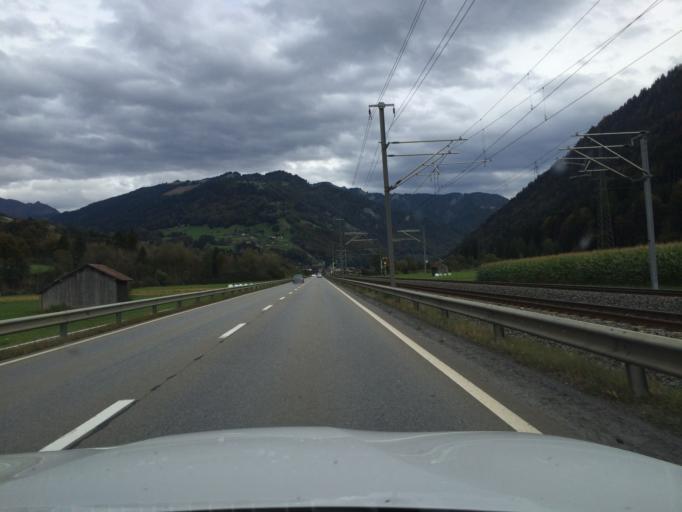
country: CH
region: Grisons
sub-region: Praettigau/Davos District
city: Schiers
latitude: 46.9749
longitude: 9.6671
